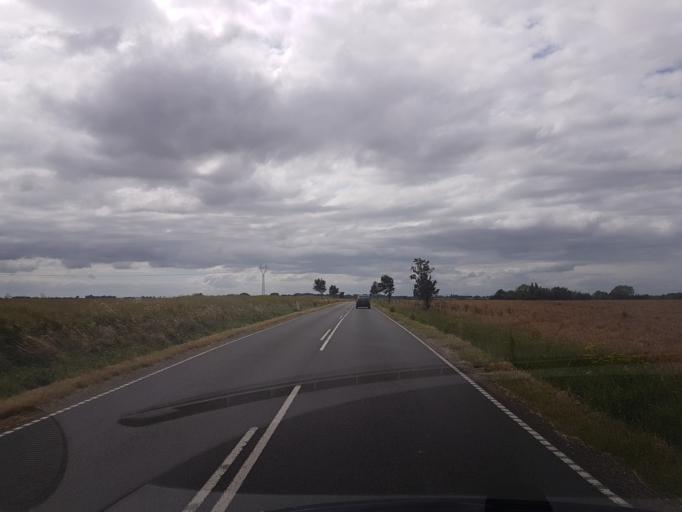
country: DK
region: South Denmark
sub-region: Nordfyns Kommune
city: Sonderso
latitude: 55.5427
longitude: 10.2587
